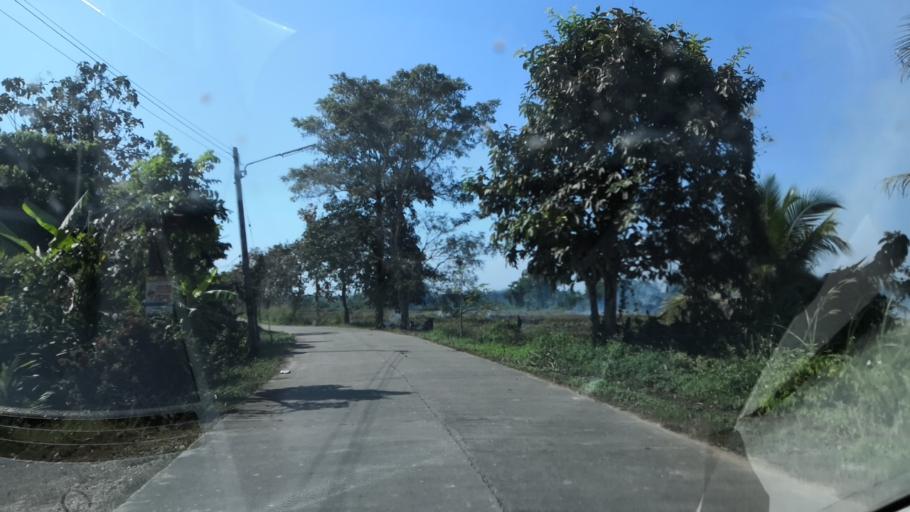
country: TH
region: Chiang Rai
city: Wiang Chai
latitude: 19.8853
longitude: 99.9450
